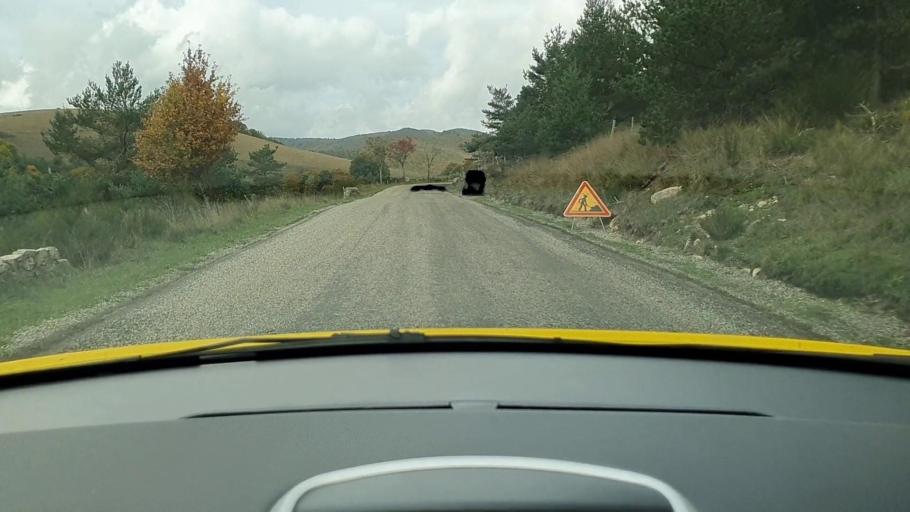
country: FR
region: Languedoc-Roussillon
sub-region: Departement du Gard
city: Valleraugue
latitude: 44.0704
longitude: 3.5381
